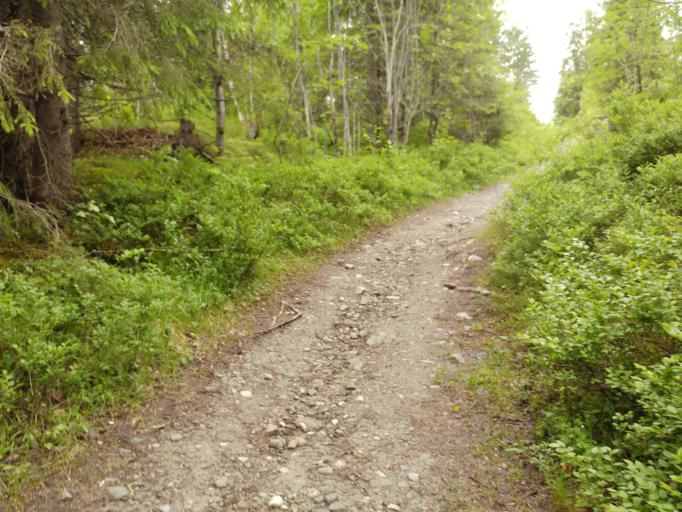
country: NO
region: Sor-Trondelag
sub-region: Melhus
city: Melhus
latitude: 63.3832
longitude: 10.3049
